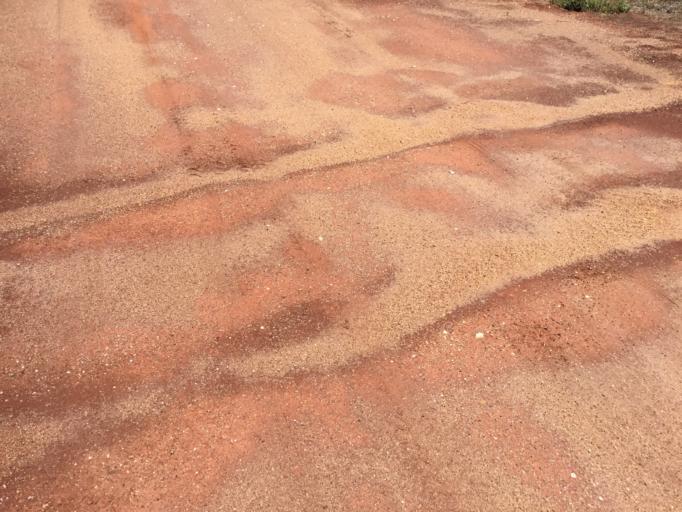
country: US
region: Kansas
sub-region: Sedgwick County
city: Cheney
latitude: 37.6191
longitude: -97.8449
